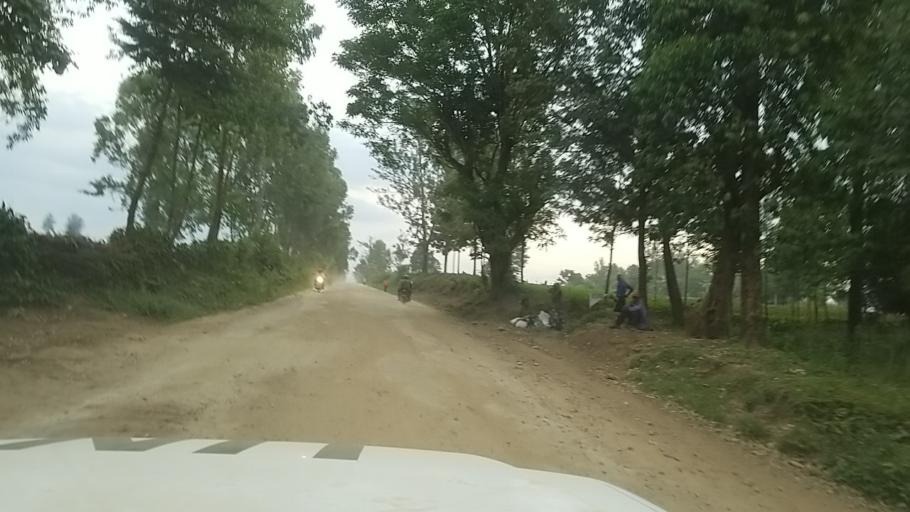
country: CD
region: South Kivu
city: Bukavu
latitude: -2.2492
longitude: 28.8260
